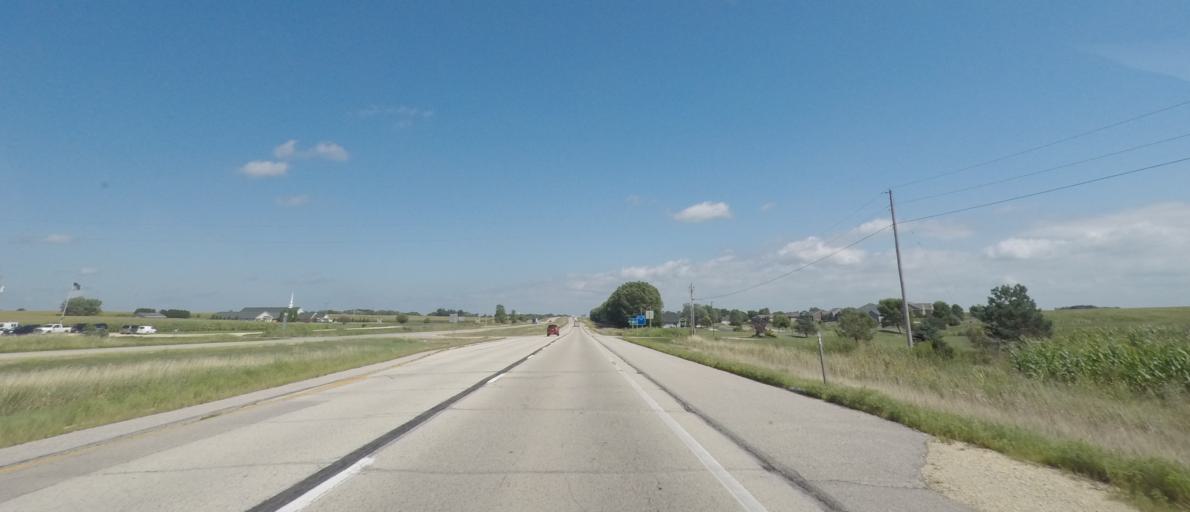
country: US
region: Iowa
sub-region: Jones County
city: Anamosa
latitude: 42.0707
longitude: -91.3511
